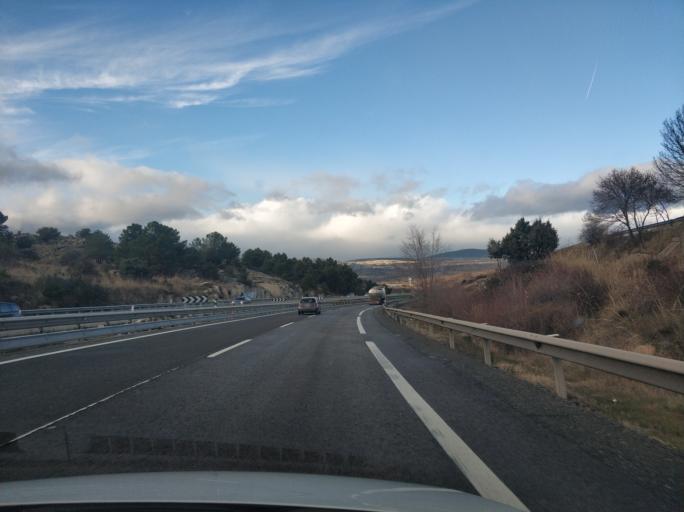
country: ES
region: Madrid
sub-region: Provincia de Madrid
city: La Cabrera
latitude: 40.8915
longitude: -3.6018
